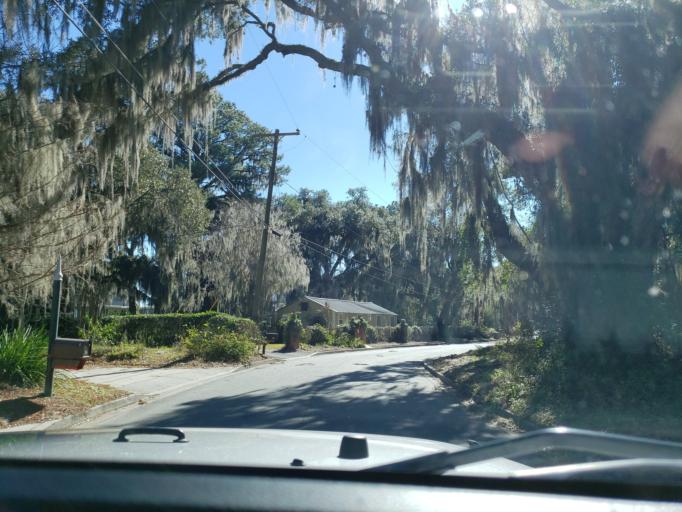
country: US
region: Georgia
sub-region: Chatham County
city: Whitemarsh Island
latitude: 32.0411
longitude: -80.9864
